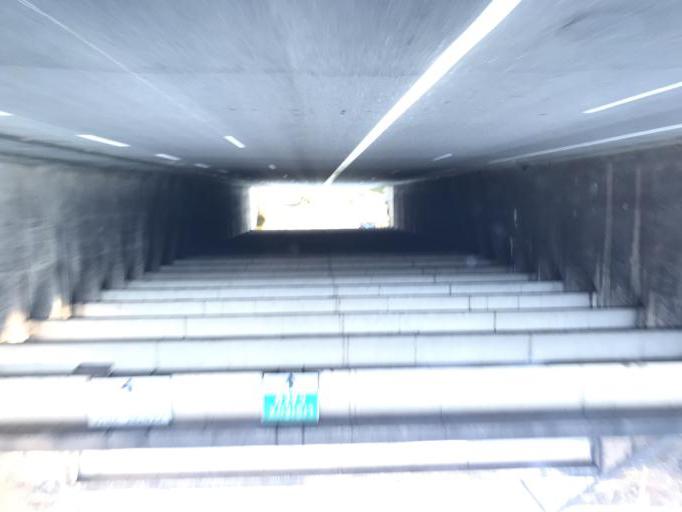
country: FR
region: Haute-Normandie
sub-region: Departement de l'Eure
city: Evreux
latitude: 49.0168
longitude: 1.1438
